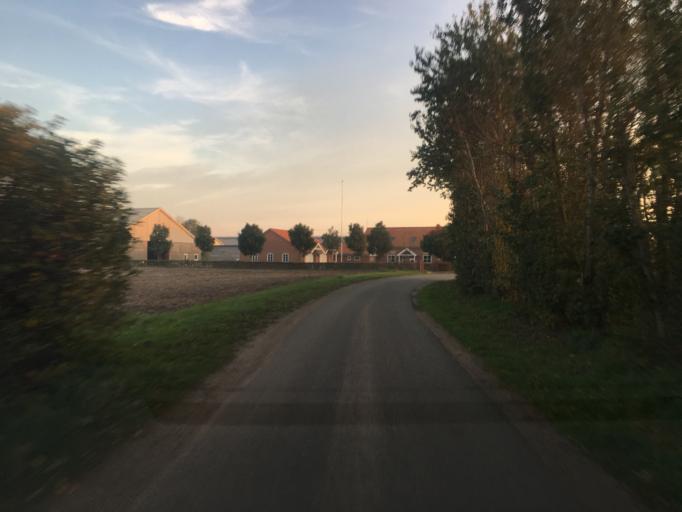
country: DE
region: Schleswig-Holstein
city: Bramstedtlund
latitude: 54.9942
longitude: 9.1012
